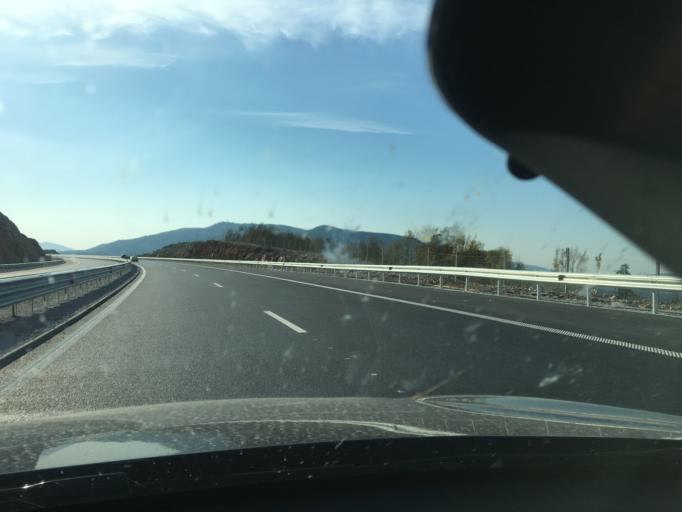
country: BG
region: Lovech
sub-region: Obshtina Yablanitsa
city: Yablanitsa
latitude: 43.0471
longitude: 24.1334
